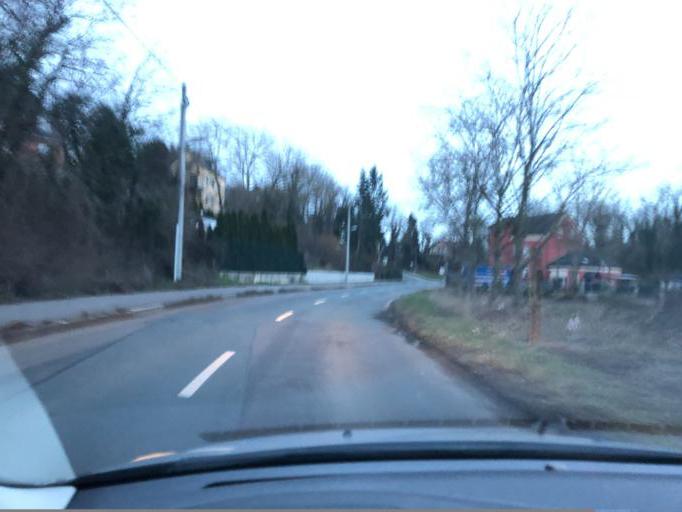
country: DE
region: Saxony-Anhalt
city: Weissenfels
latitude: 51.2147
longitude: 11.9564
